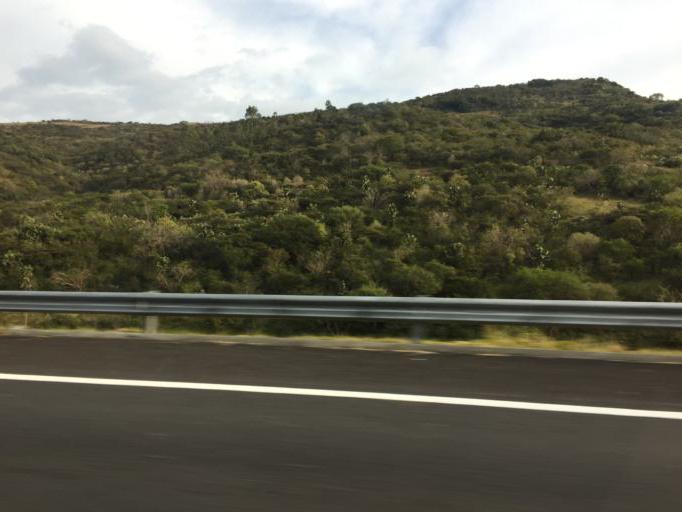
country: MX
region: Michoacan
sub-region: Cuitzeo
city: San Juan Benito Juarez (San Juan Tararameo)
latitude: 19.8927
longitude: -101.1625
